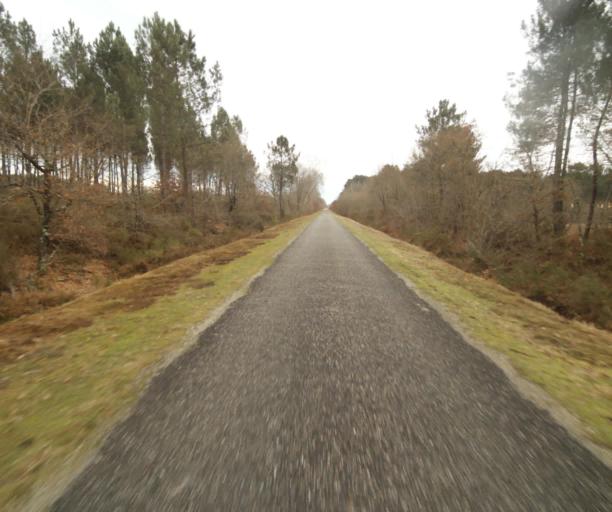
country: FR
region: Aquitaine
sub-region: Departement des Landes
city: Gabarret
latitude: 44.0232
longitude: -0.0486
